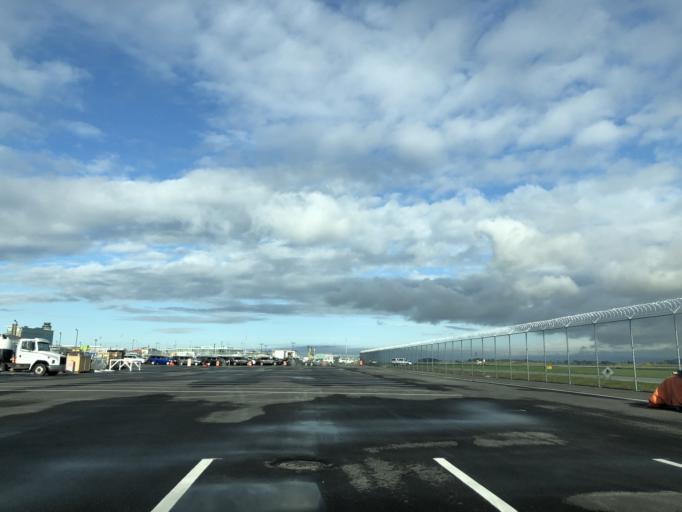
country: CA
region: British Columbia
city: Richmond
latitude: 49.1976
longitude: -123.1617
